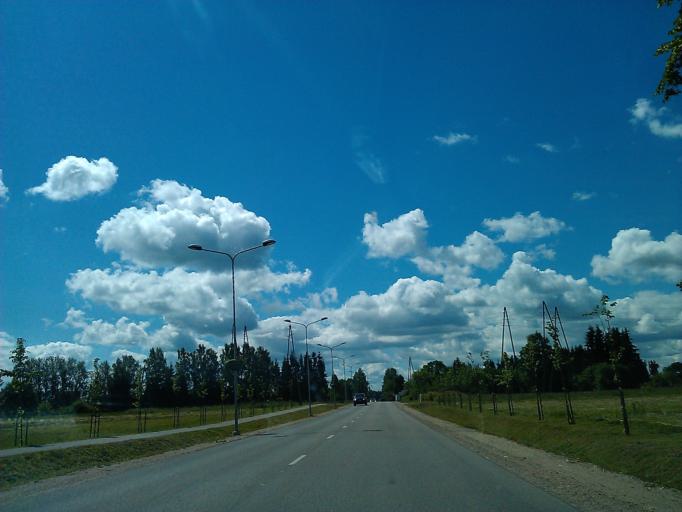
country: LV
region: Vilanu
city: Vilani
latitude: 56.5641
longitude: 26.9281
